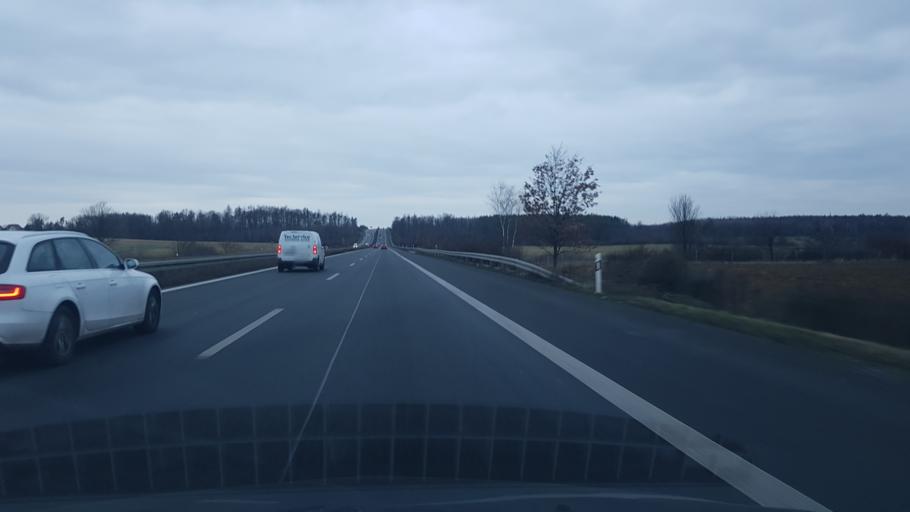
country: DE
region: Saxony
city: Wachau
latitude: 51.1713
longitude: 13.8929
